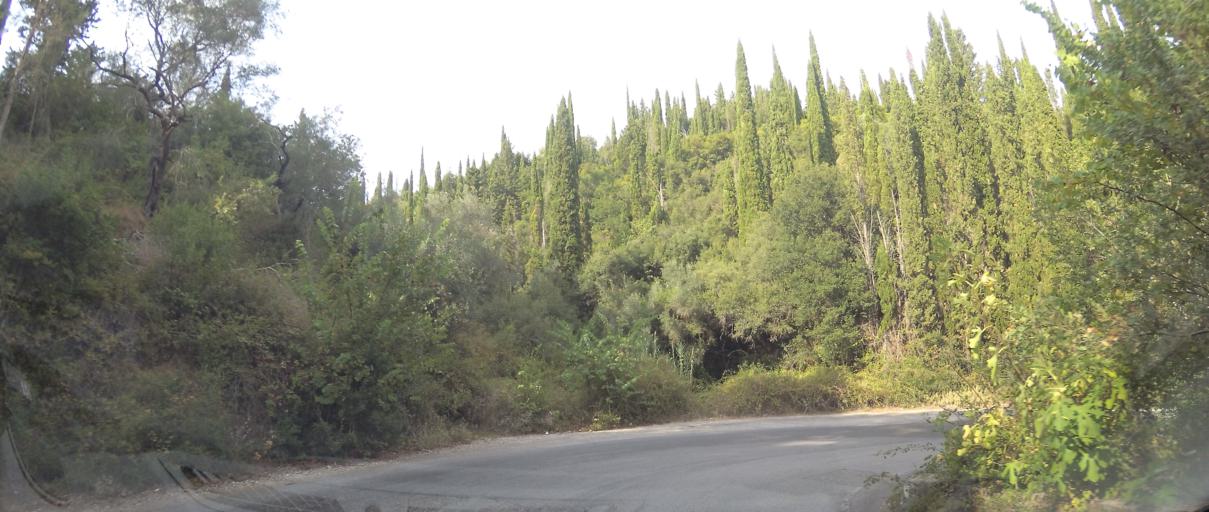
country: GR
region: Ionian Islands
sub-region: Nomos Kerkyras
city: Kynopiastes
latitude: 39.5642
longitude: 19.8717
